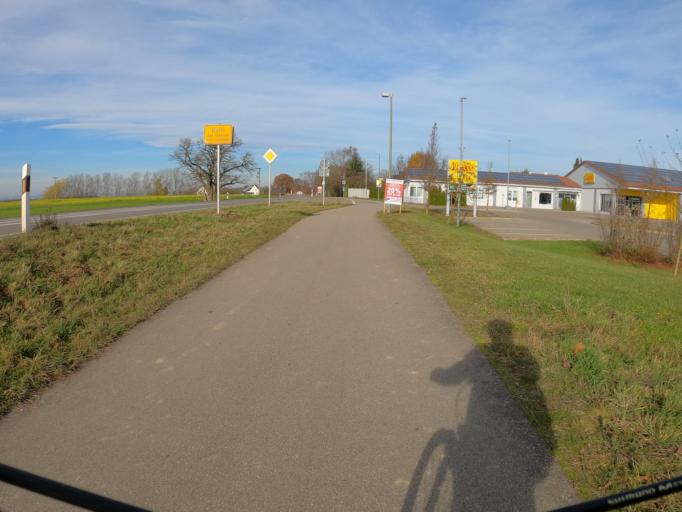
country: DE
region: Bavaria
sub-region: Swabia
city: Leipheim
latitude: 48.4128
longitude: 10.1933
